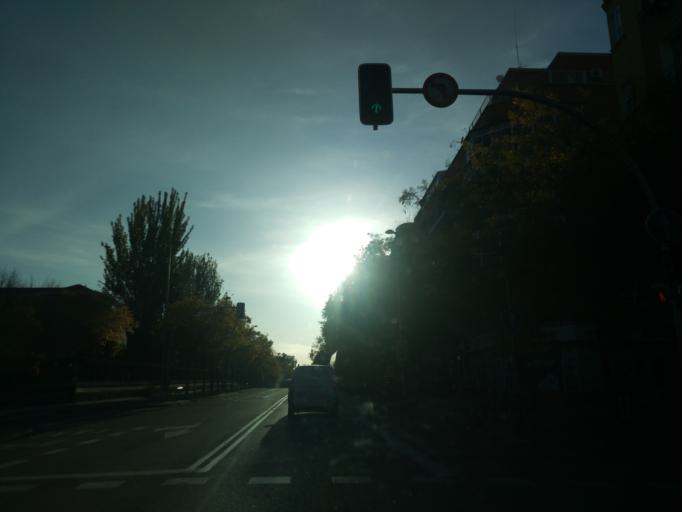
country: ES
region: Madrid
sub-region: Provincia de Madrid
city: Latina
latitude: 40.3866
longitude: -3.7347
